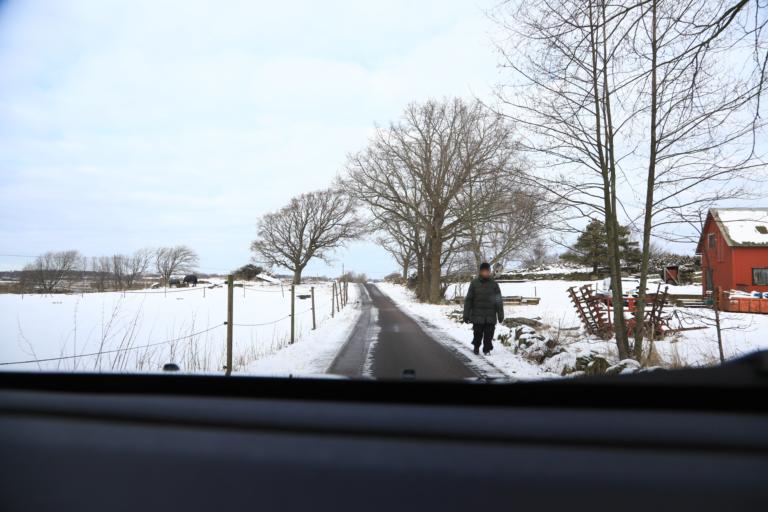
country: SE
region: Halland
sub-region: Kungsbacka Kommun
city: Frillesas
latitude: 57.2315
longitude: 12.1910
